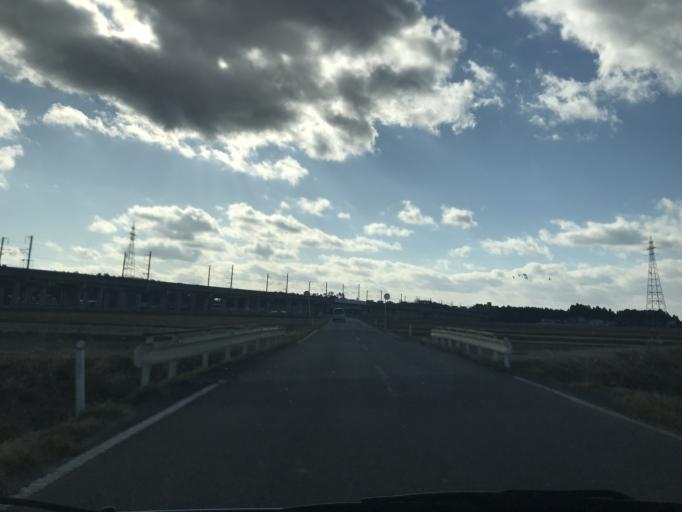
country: JP
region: Iwate
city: Ichinoseki
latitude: 38.7426
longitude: 141.0664
